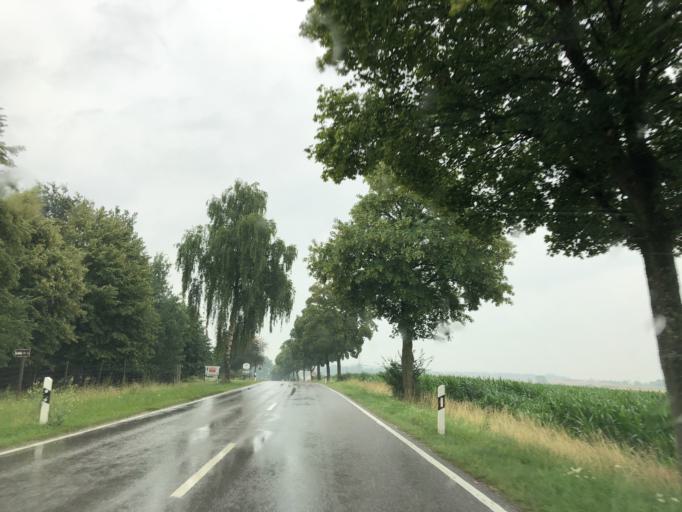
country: DE
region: Bavaria
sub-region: Upper Bavaria
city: Wolfersdorf
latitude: 48.5330
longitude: 11.7562
